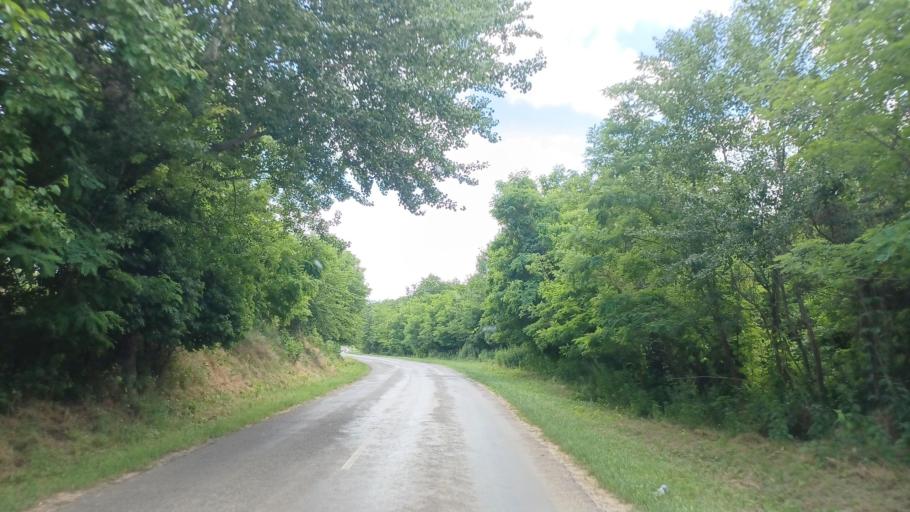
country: HU
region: Tolna
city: Simontornya
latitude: 46.7194
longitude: 18.4980
